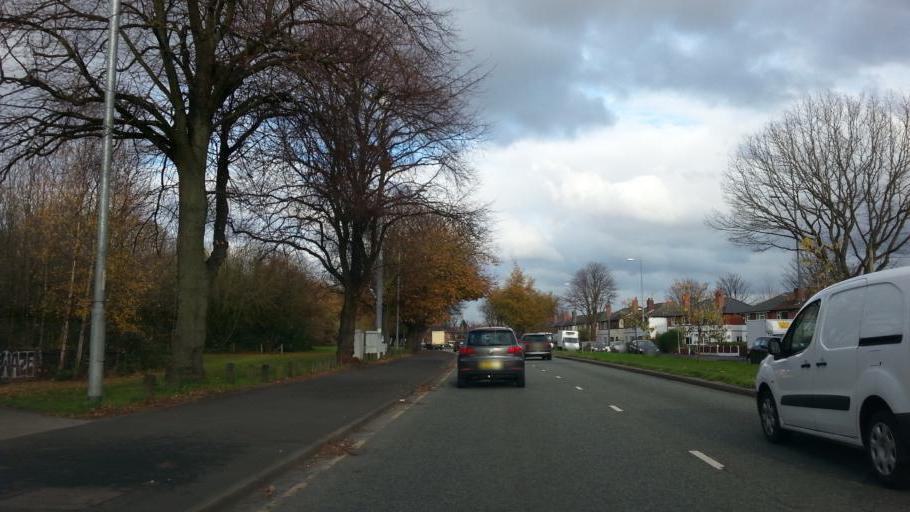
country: GB
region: England
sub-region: Manchester
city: Chorlton cum Hardy
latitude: 53.4364
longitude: -2.2451
